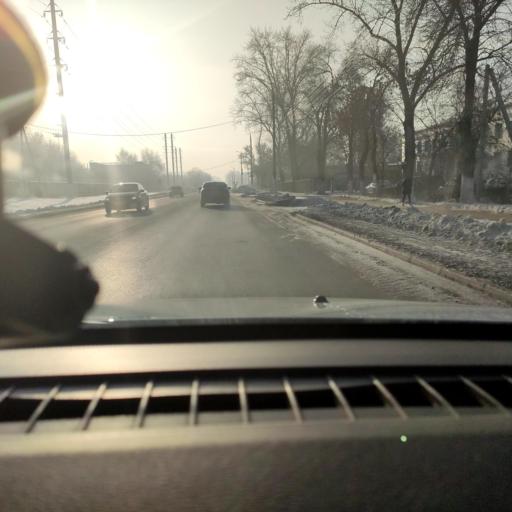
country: RU
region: Samara
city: Chapayevsk
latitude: 52.9676
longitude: 49.7019
